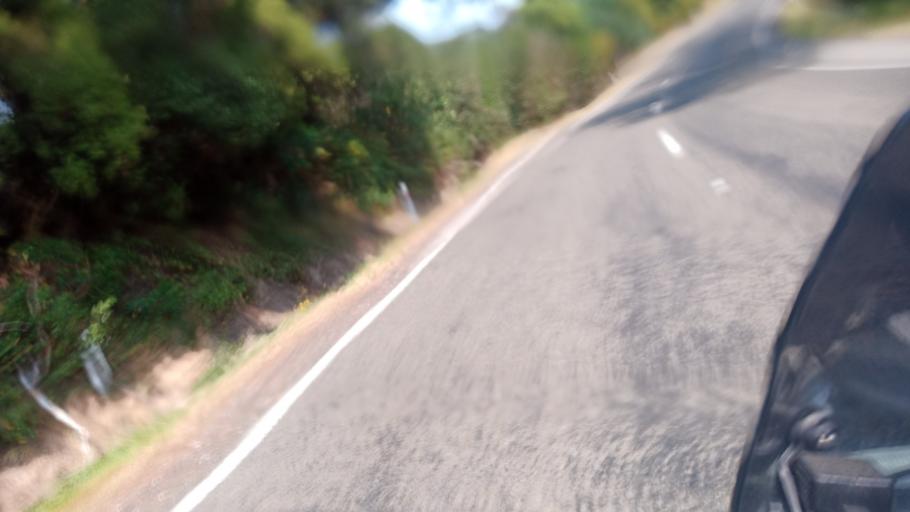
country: NZ
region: Bay of Plenty
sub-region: Opotiki District
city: Opotiki
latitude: -37.5909
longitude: 178.2320
